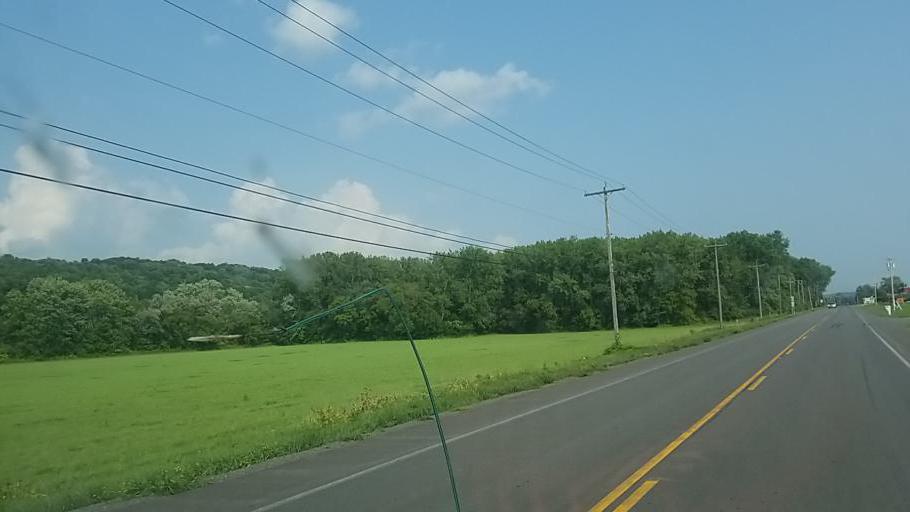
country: US
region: New York
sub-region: Montgomery County
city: Fonda
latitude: 42.9474
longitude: -74.3544
